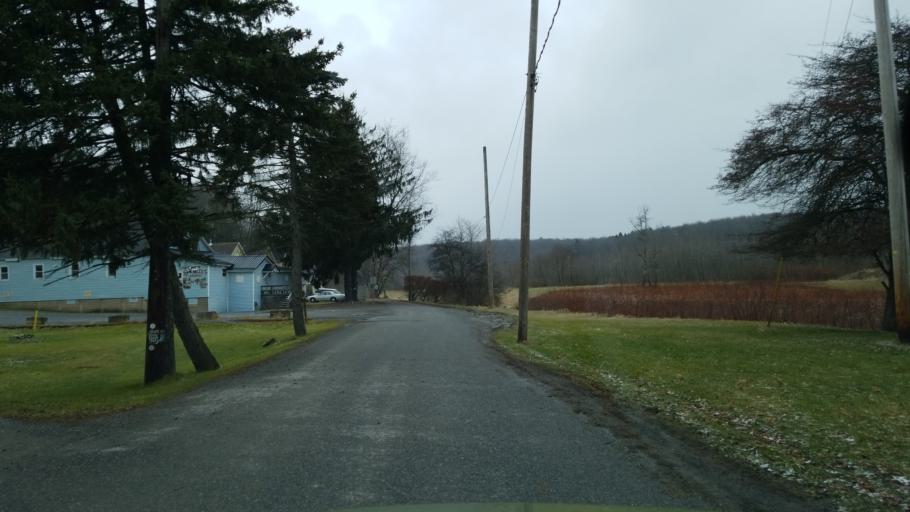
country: US
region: Pennsylvania
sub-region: Clearfield County
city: DuBois
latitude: 41.1258
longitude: -78.7686
